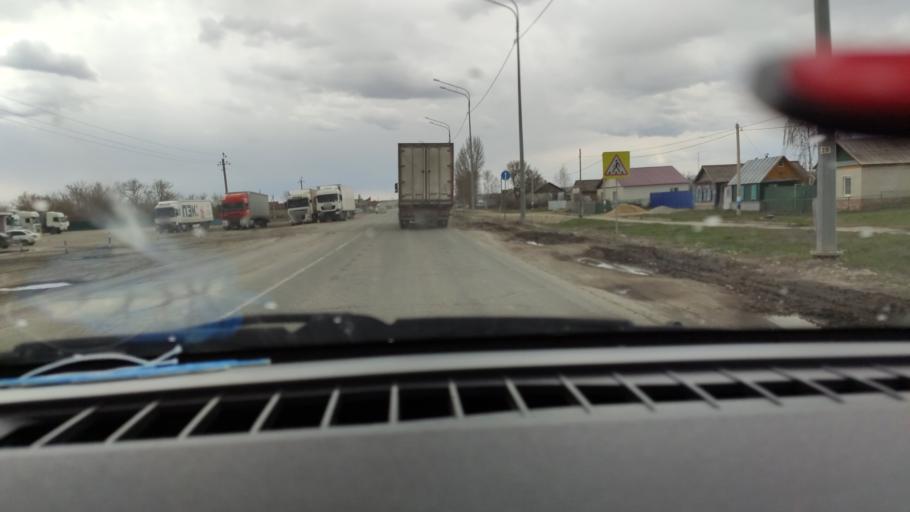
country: RU
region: Saratov
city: Sinodskoye
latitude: 51.9835
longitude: 46.6611
